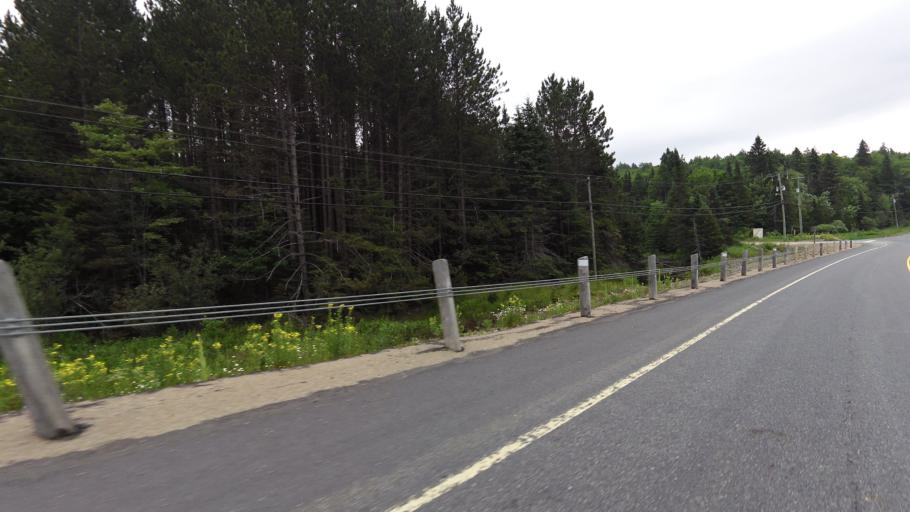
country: CA
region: Ontario
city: Huntsville
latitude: 45.5417
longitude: -78.6967
